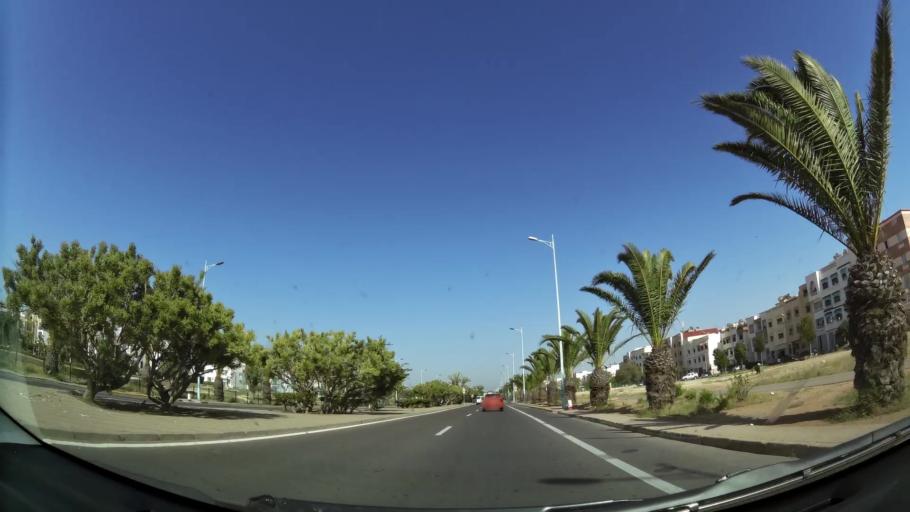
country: MA
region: Oued ed Dahab-Lagouira
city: Dakhla
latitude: 30.4035
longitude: -9.5543
